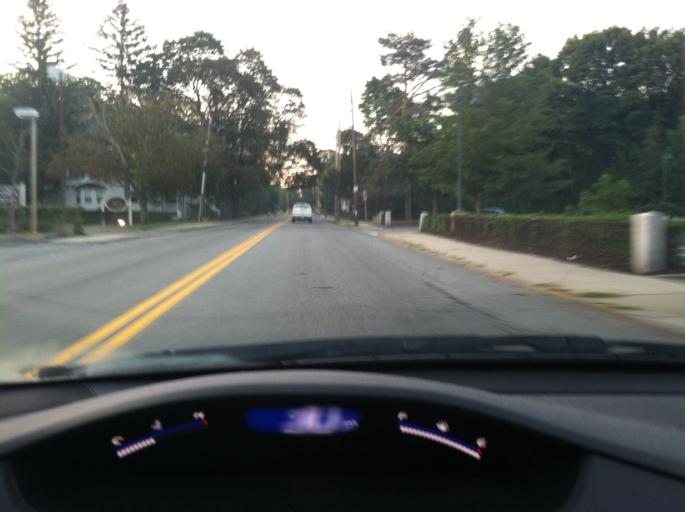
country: US
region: Massachusetts
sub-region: Middlesex County
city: Lexington
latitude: 42.4576
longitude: -71.2368
